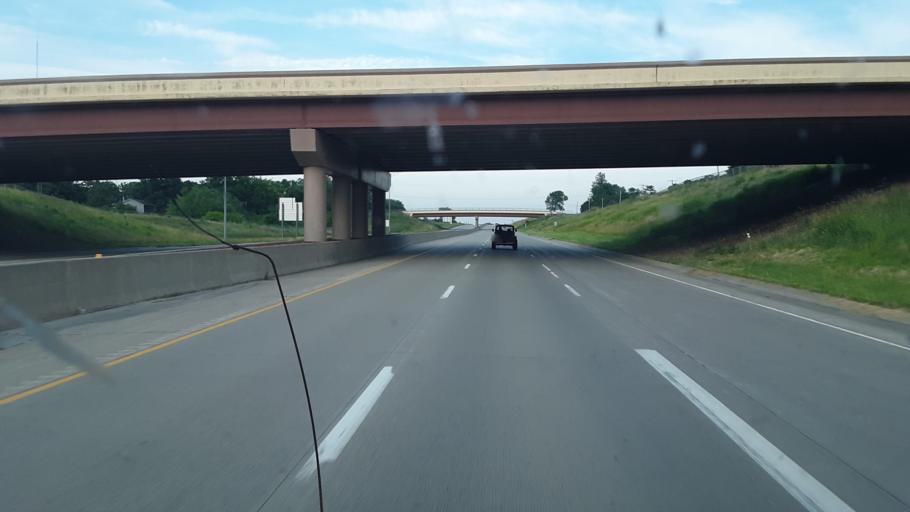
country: US
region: Iowa
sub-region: Tama County
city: Toledo
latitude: 41.9822
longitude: -92.5819
